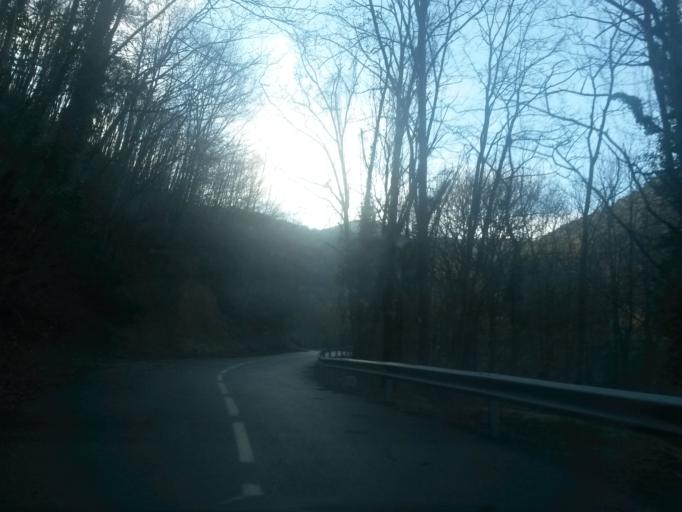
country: ES
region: Catalonia
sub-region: Provincia de Girona
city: Sant Hilari Sacalm
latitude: 41.9271
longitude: 2.5130
